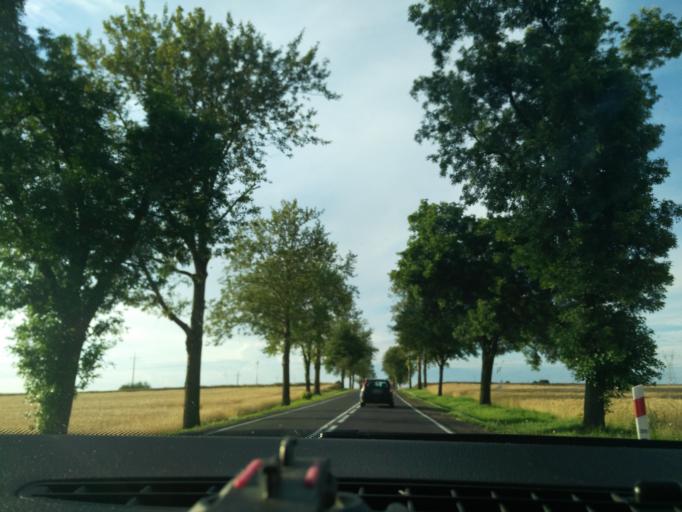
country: PL
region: Lublin Voivodeship
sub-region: Powiat krasnicki
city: Szastarka
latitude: 50.8108
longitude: 22.3195
